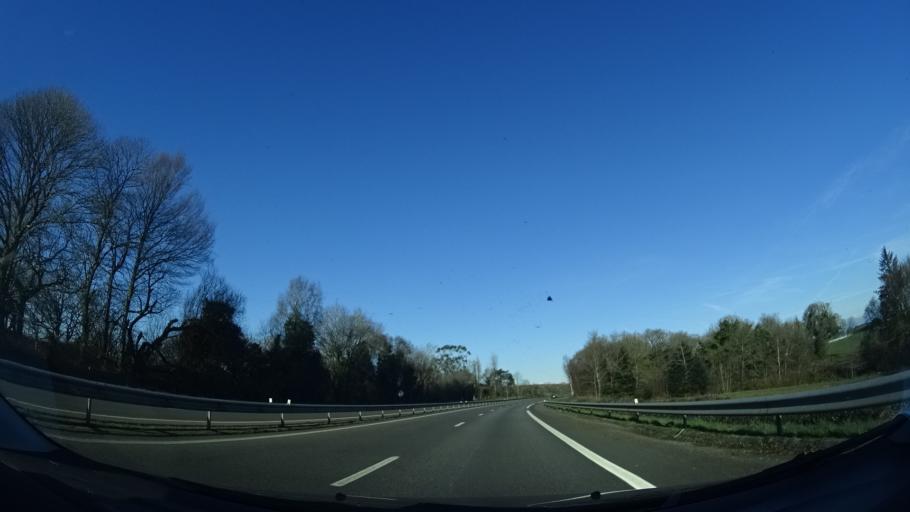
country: FR
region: Brittany
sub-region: Departement du Finistere
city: Taule
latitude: 48.5945
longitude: -3.8883
